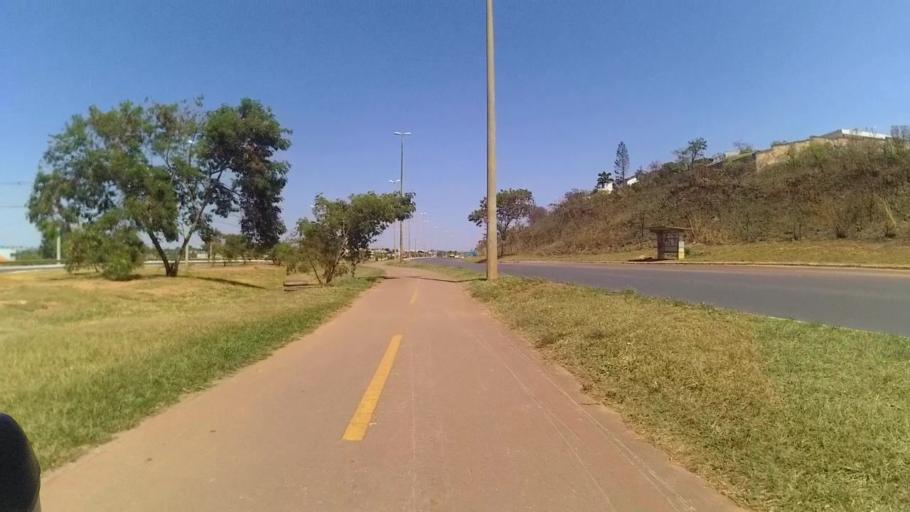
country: BR
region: Federal District
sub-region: Brasilia
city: Brasilia
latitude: -15.7211
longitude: -47.8516
